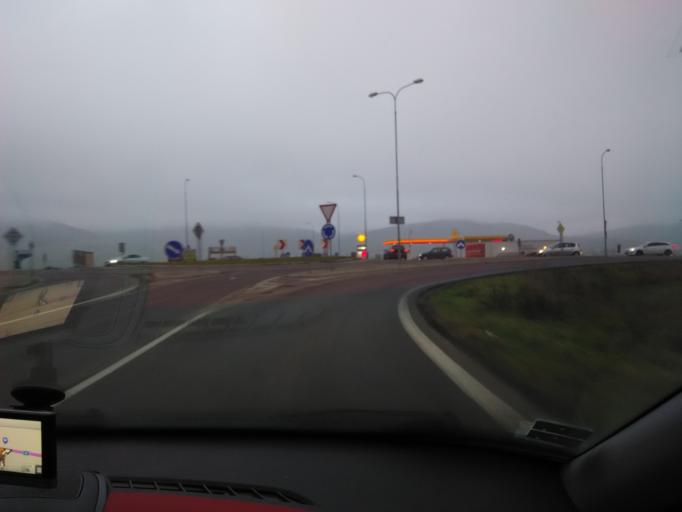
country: SK
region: Nitriansky
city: Dubnica nad Vahom
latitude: 48.9526
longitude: 18.1500
